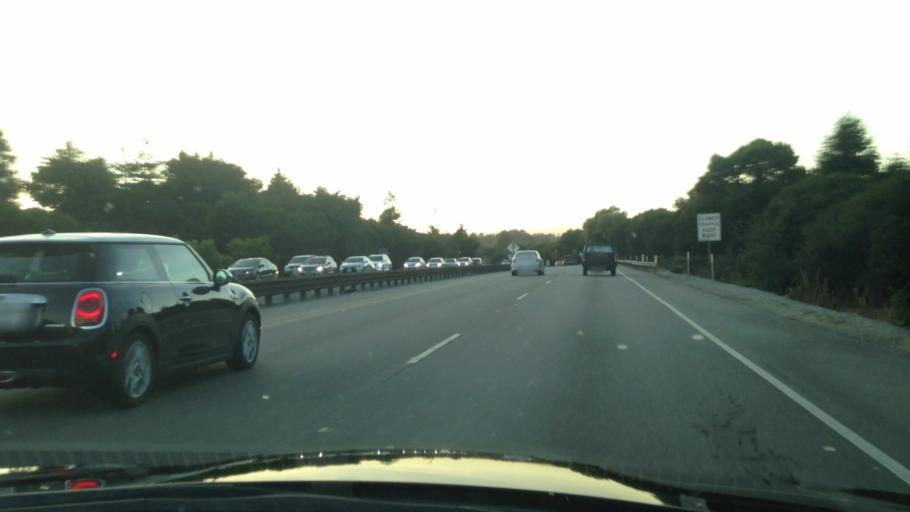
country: US
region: California
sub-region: Santa Cruz County
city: Seacliff
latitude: 36.9801
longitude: -121.9143
